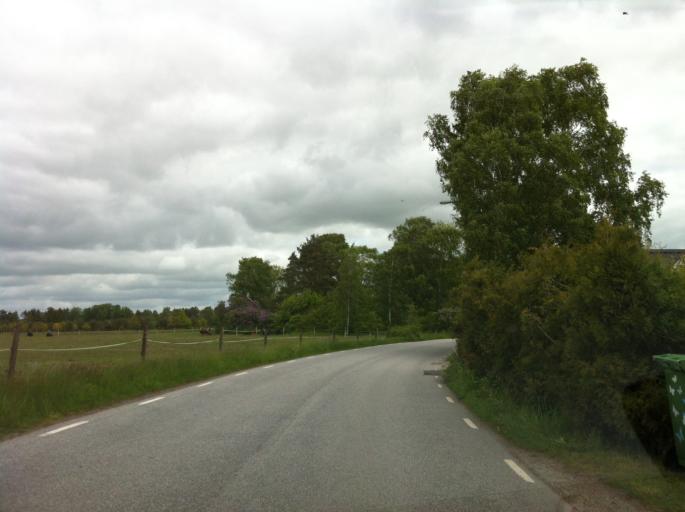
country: SE
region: Skane
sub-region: Kavlinge Kommun
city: Loddekopinge
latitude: 55.8057
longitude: 13.0398
